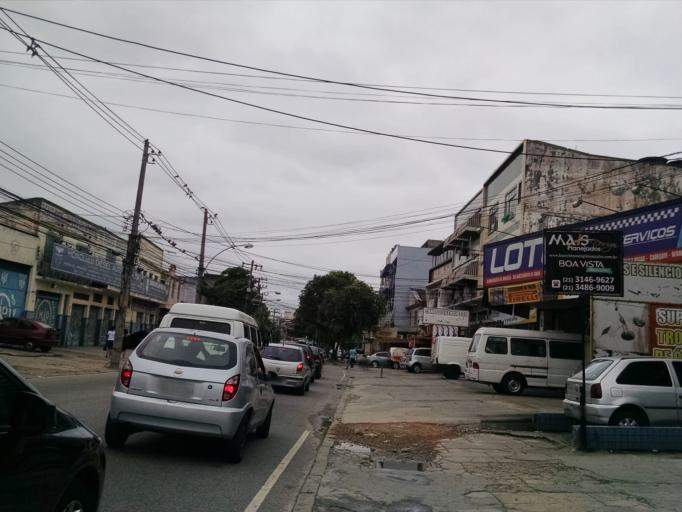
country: BR
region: Rio de Janeiro
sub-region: Duque De Caxias
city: Duque de Caxias
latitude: -22.8304
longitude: -43.3191
